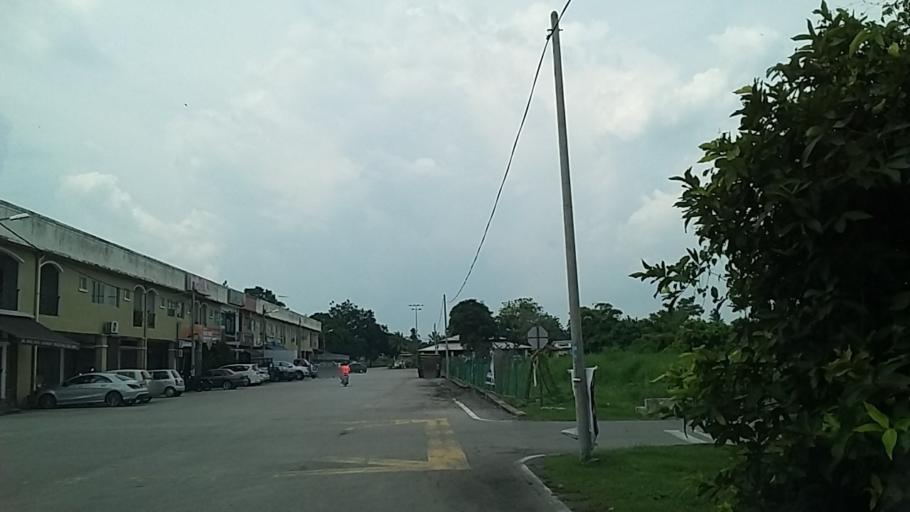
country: MY
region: Johor
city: Parit Raja
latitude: 1.7475
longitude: 103.0507
